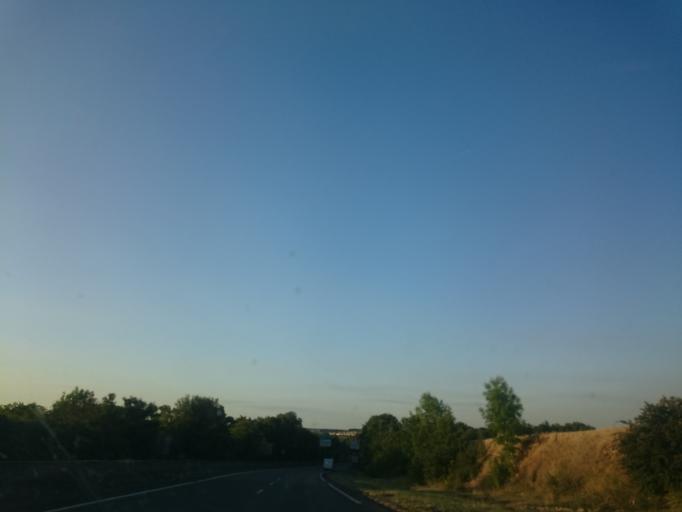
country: FR
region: Ile-de-France
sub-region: Departement de l'Essonne
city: Etampes
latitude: 48.4146
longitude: 2.1297
